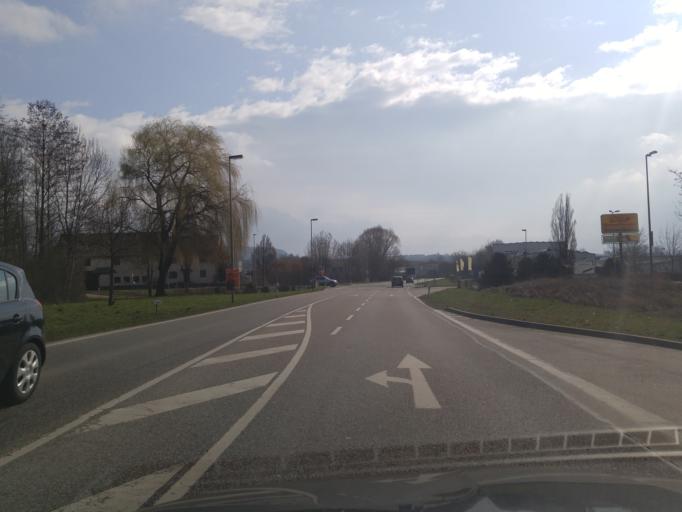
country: DE
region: Baden-Wuerttemberg
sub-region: Regierungsbezirk Stuttgart
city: Abstatt
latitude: 49.0562
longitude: 9.2763
